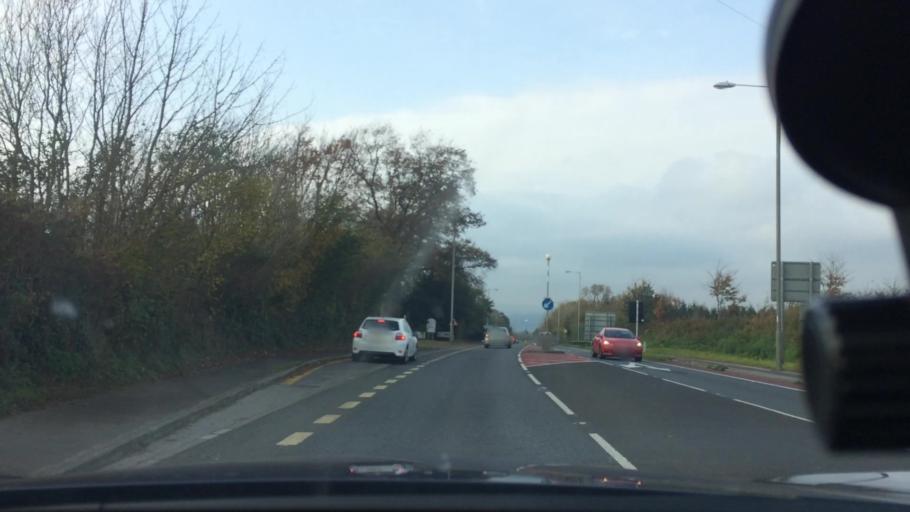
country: GB
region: England
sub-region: Devon
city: Axminster
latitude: 50.7628
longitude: -2.9694
